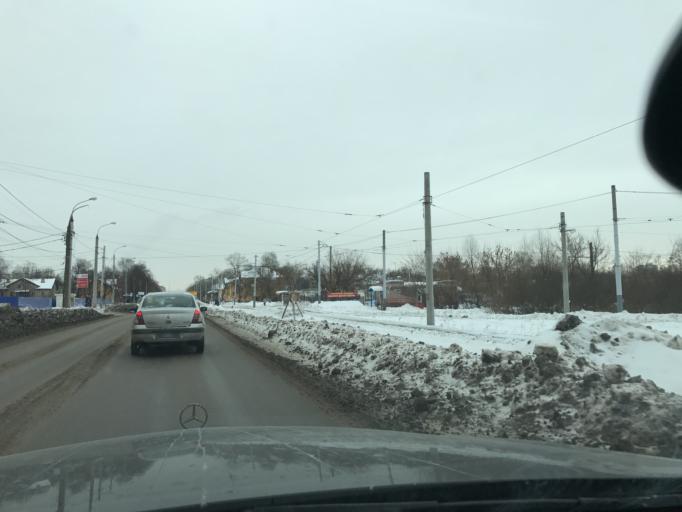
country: RU
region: Nizjnij Novgorod
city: Gorbatovka
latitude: 56.2452
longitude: 43.8247
